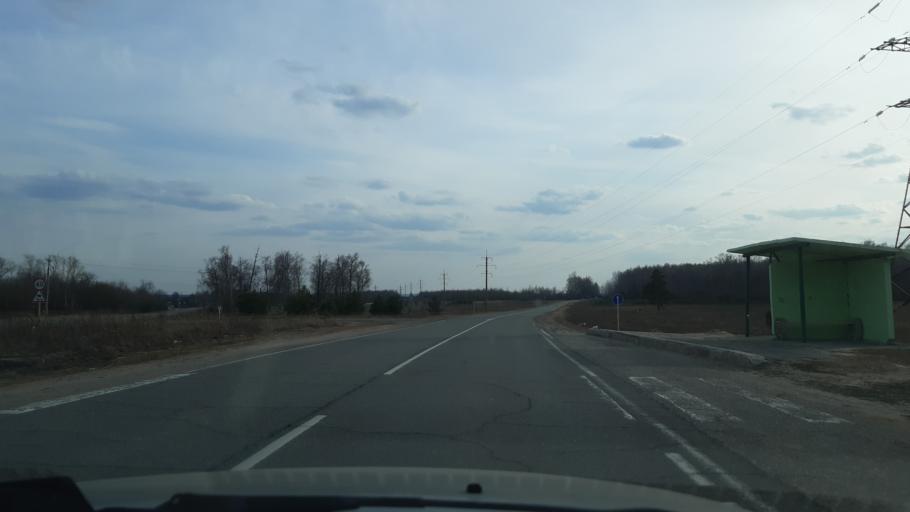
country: RU
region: Vladimir
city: Luknovo
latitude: 56.1982
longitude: 42.0337
